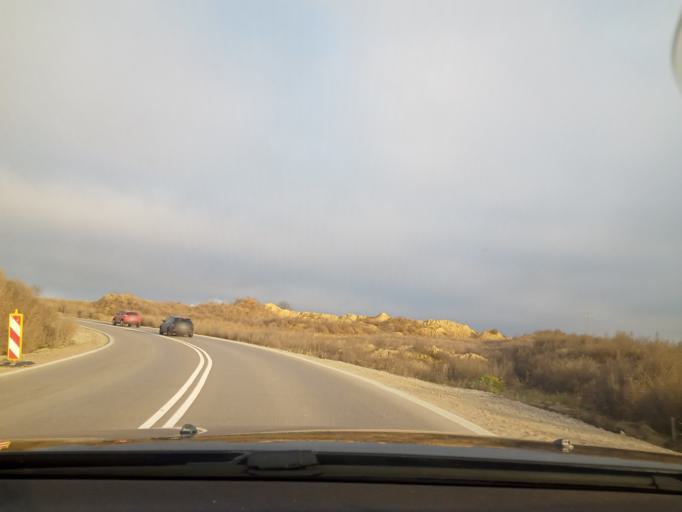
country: PL
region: Lesser Poland Voivodeship
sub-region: Powiat miechowski
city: Miechow
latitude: 50.3177
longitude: 20.0397
